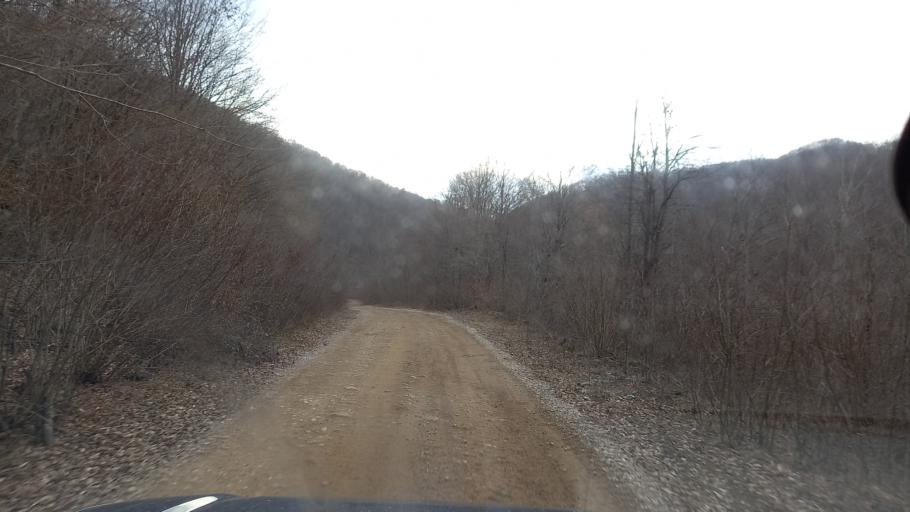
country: RU
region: Adygeya
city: Kamennomostskiy
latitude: 44.1675
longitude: 40.2993
